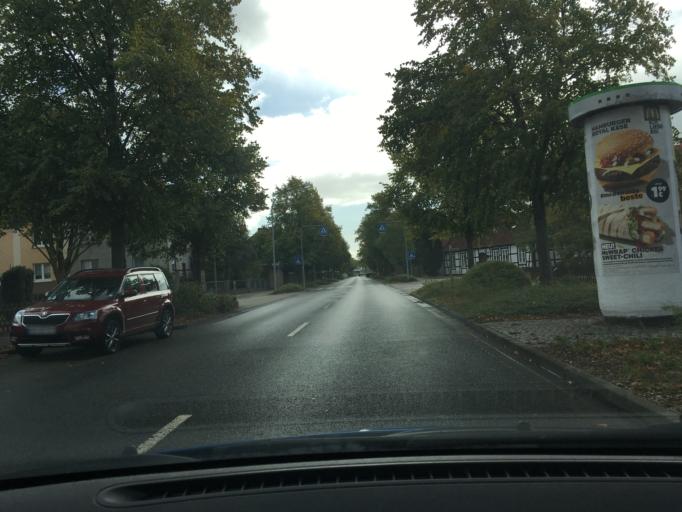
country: DE
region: Lower Saxony
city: Uelzen
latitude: 52.9703
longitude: 10.5720
